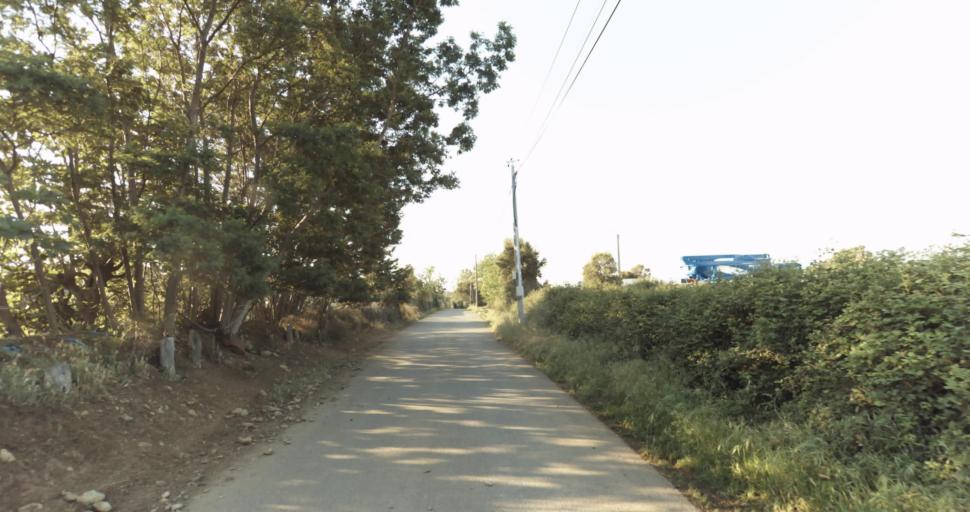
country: FR
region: Corsica
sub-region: Departement de la Haute-Corse
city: Biguglia
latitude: 42.6043
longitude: 9.4529
